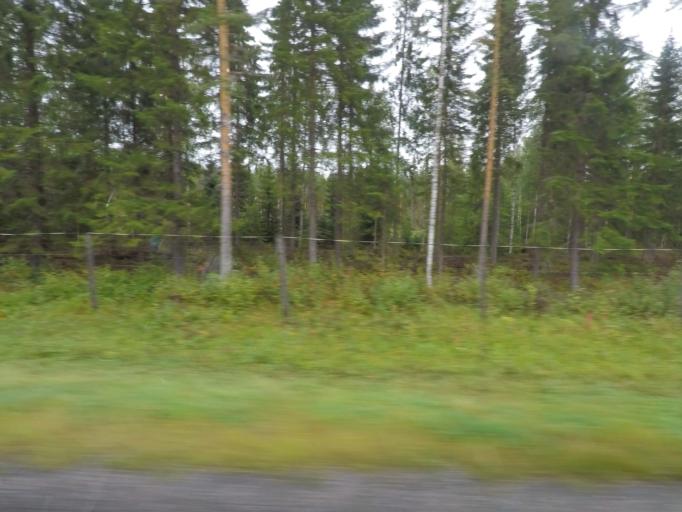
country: FI
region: Southern Savonia
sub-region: Pieksaemaeki
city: Juva
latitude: 61.9938
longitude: 27.8028
